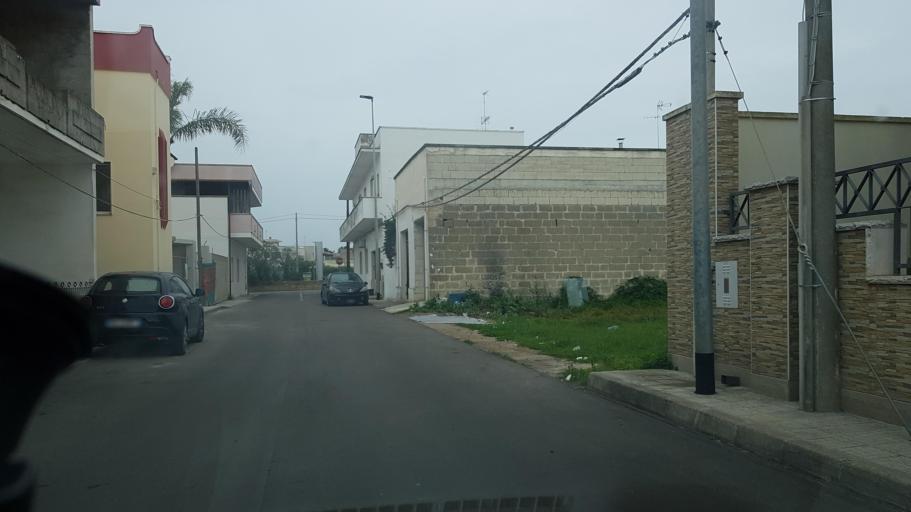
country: IT
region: Apulia
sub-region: Provincia di Lecce
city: Leverano
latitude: 40.2879
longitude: 18.0060
